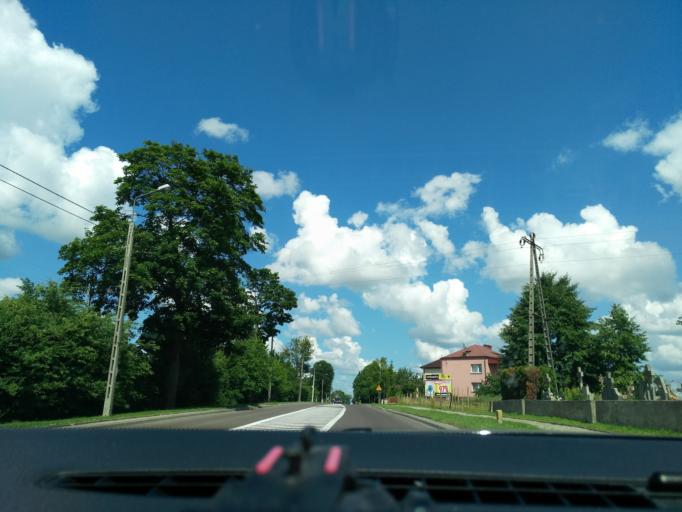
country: PL
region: Podlasie
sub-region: Powiat siemiatycki
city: Siemiatycze
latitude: 52.4332
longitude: 22.8599
